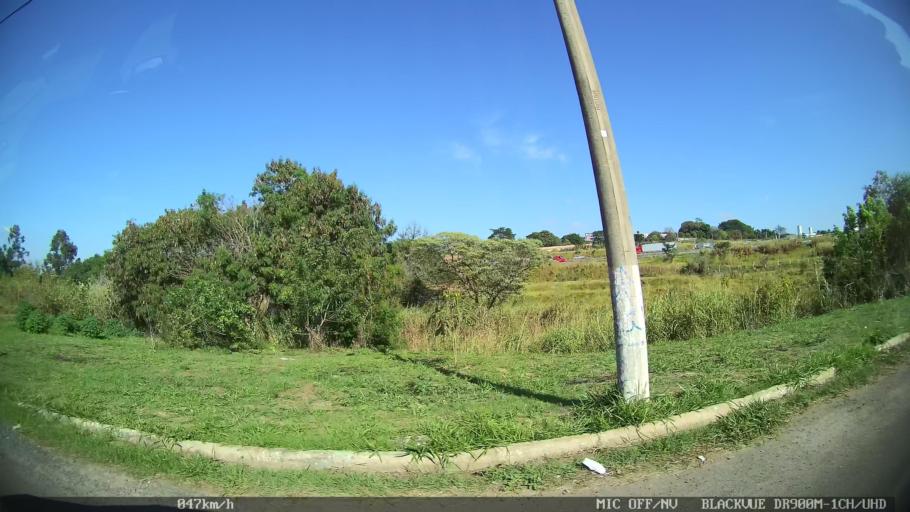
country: BR
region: Sao Paulo
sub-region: Campinas
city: Campinas
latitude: -22.9493
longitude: -47.1244
